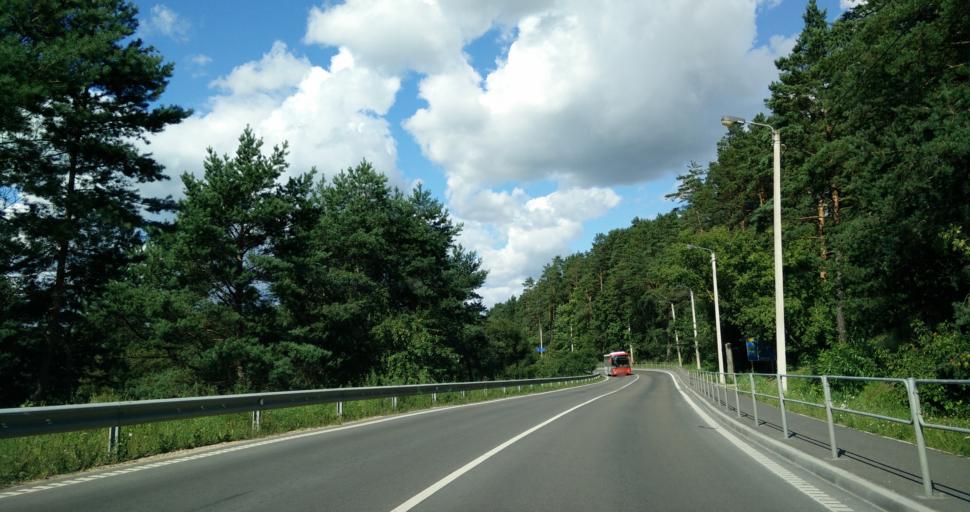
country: LT
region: Kauno apskritis
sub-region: Kauno rajonas
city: Akademija (Kaunas)
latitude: 54.9250
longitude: 23.7932
